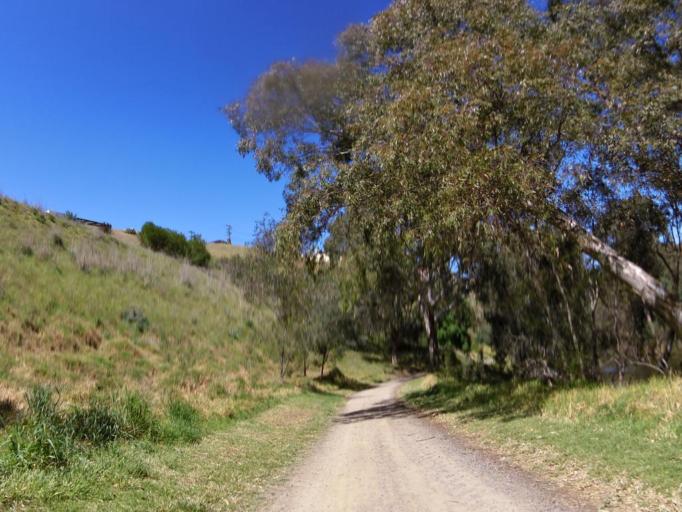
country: AU
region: Victoria
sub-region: Brimbank
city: Albion
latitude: -37.7640
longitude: 144.8544
